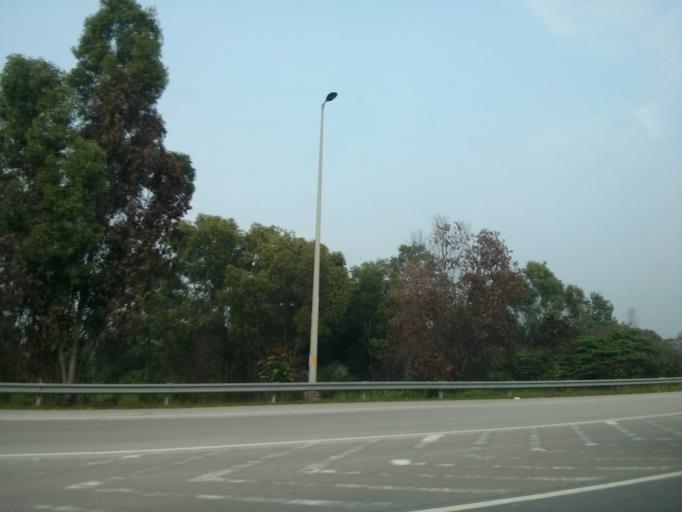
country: MY
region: Putrajaya
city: Putrajaya
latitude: 2.8781
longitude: 101.6653
